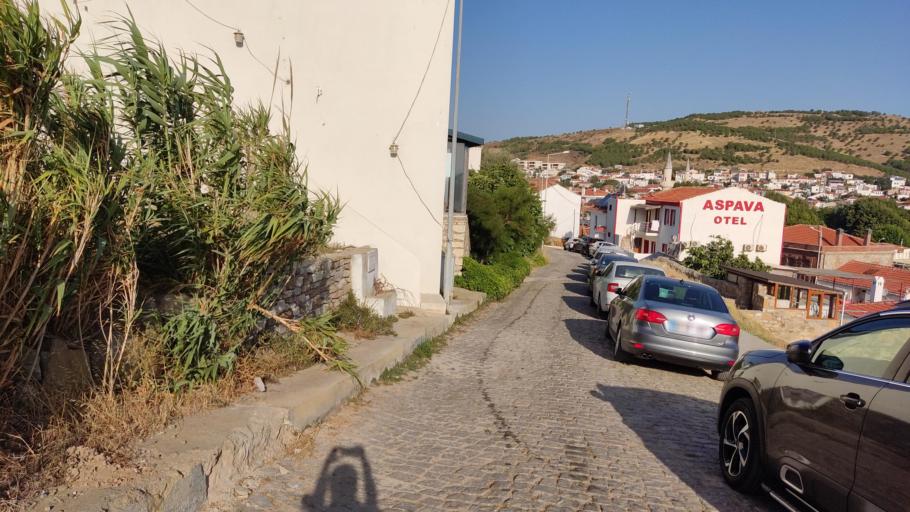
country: TR
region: Canakkale
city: Bozcaada
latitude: 39.8331
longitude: 26.0740
